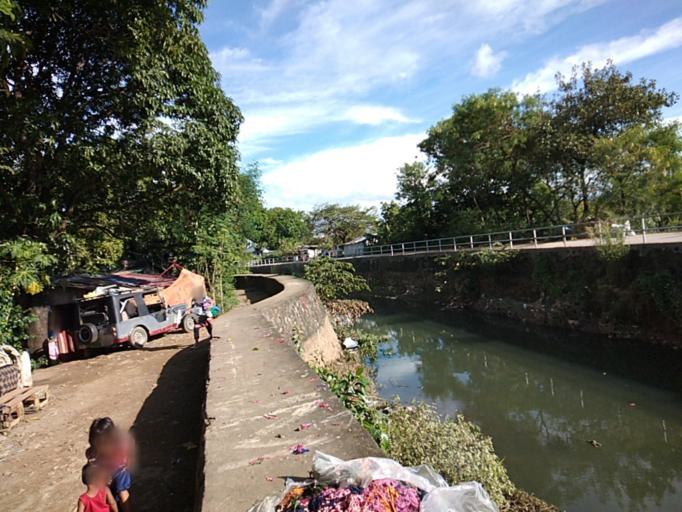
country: PH
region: Calabarzon
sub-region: Province of Rizal
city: Taytay
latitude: 14.5598
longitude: 121.1263
